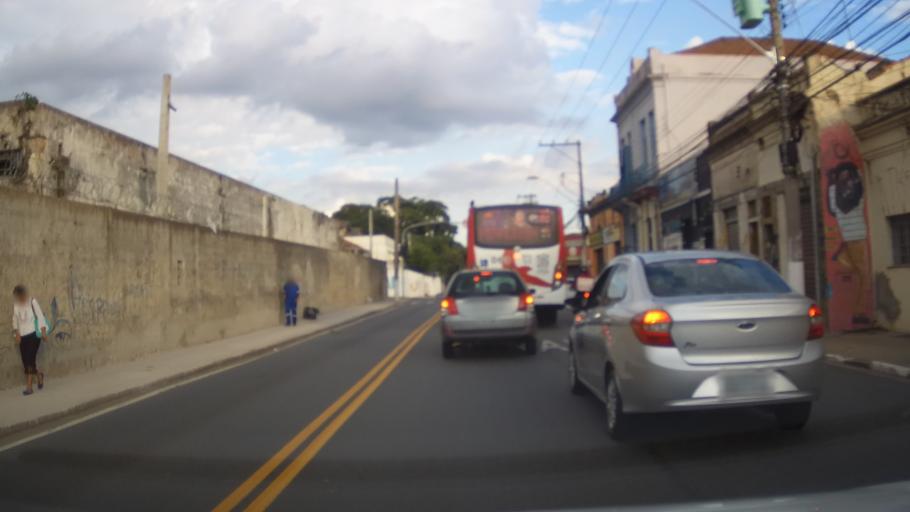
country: BR
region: Sao Paulo
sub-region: Campinas
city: Campinas
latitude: -22.9093
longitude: -47.0734
